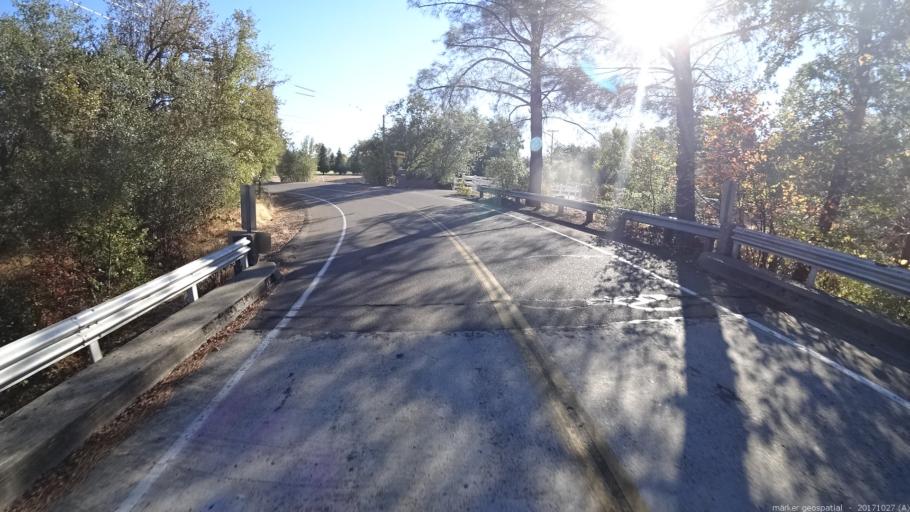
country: US
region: California
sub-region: Shasta County
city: Palo Cedro
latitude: 40.5529
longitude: -122.1841
